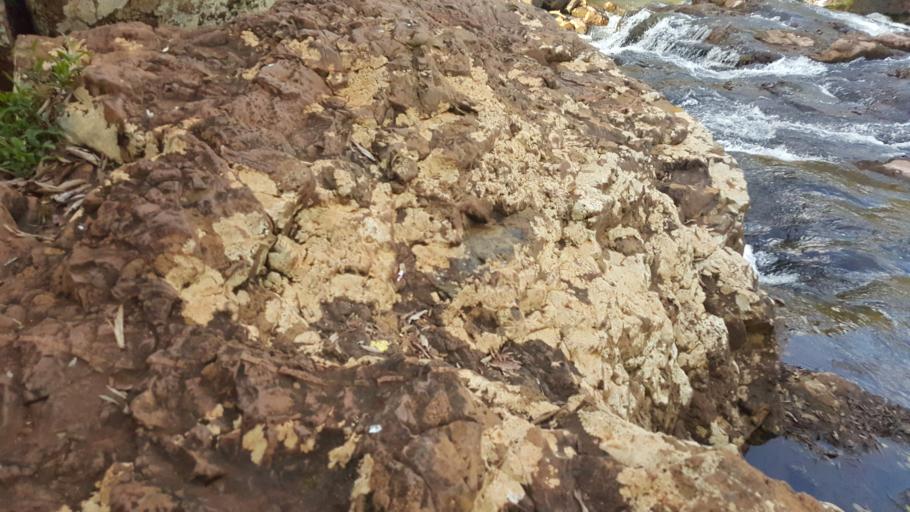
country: AR
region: Misiones
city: Puerto Leoni
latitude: -26.9994
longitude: -55.1780
